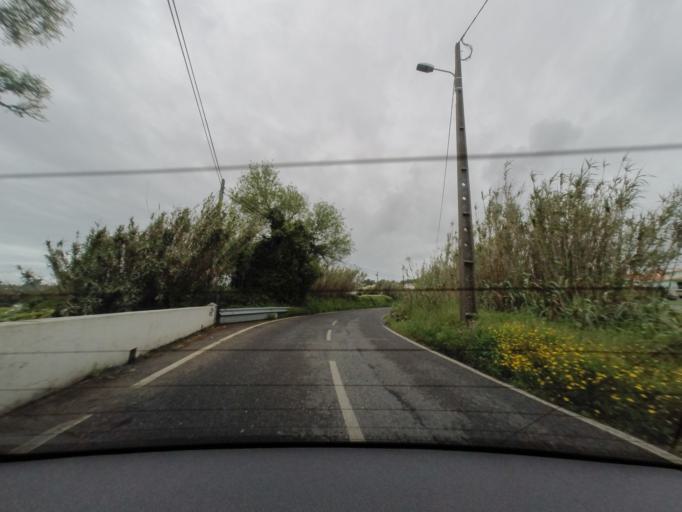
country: PT
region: Lisbon
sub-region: Sintra
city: Sintra
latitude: 38.8125
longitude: -9.3904
